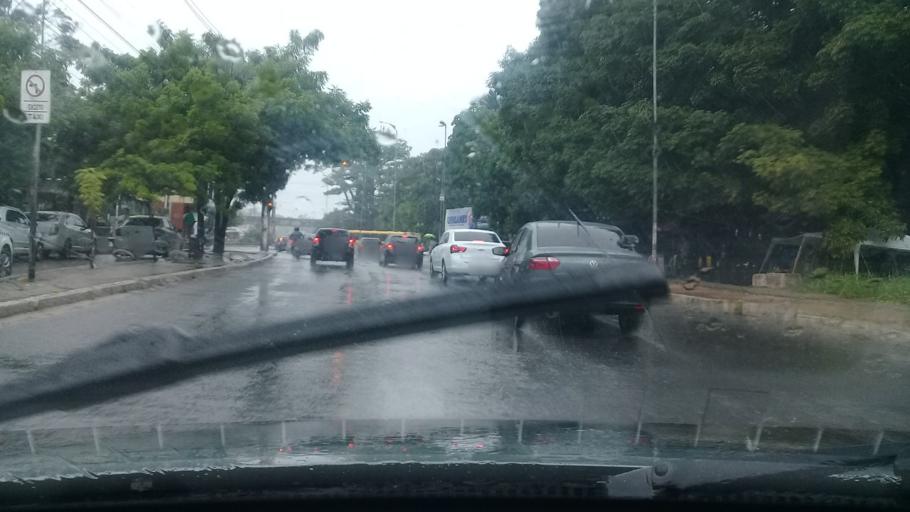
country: BR
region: Pernambuco
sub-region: Paulista
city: Paulista
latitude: -7.9468
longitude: -34.8782
